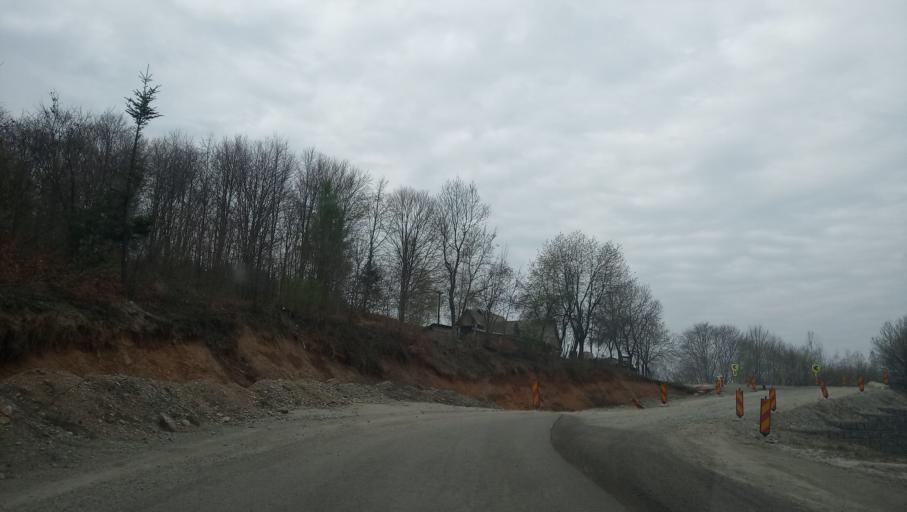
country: RO
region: Bihor
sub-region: Comuna Cristioru de Jos
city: Cristioru de Jos
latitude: 46.3959
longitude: 22.5557
